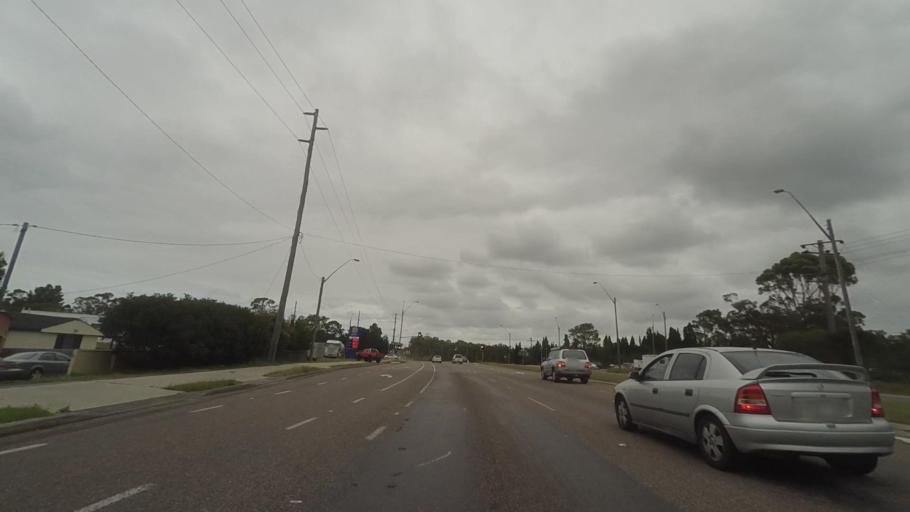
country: AU
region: New South Wales
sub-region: Wyong Shire
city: Buff Point
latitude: -33.1988
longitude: 151.5234
